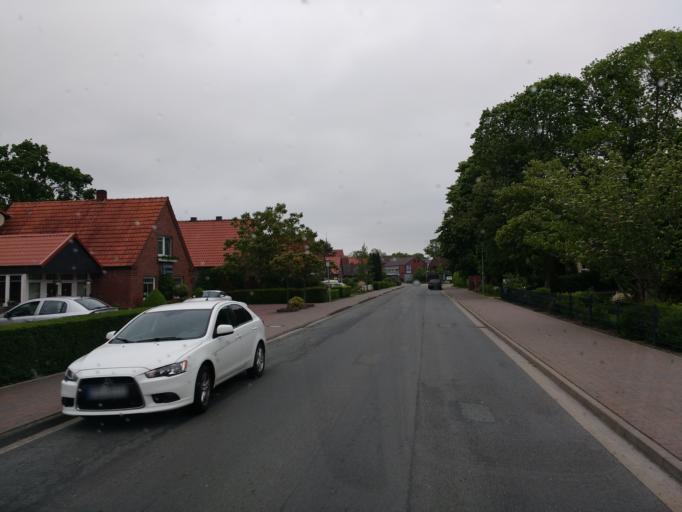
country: DE
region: Lower Saxony
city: Jever
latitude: 53.6594
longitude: 7.9160
